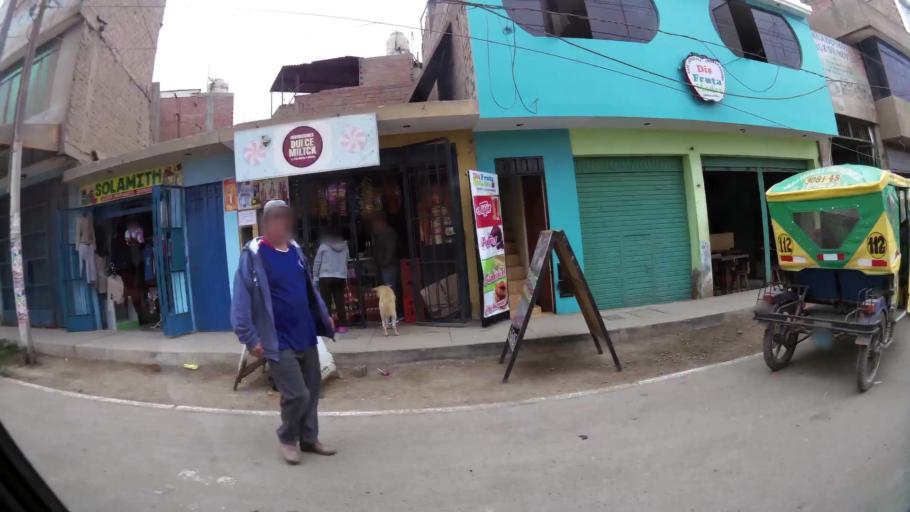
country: PE
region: Lima
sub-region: Lima
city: Urb. Santo Domingo
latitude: -11.8884
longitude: -77.0660
